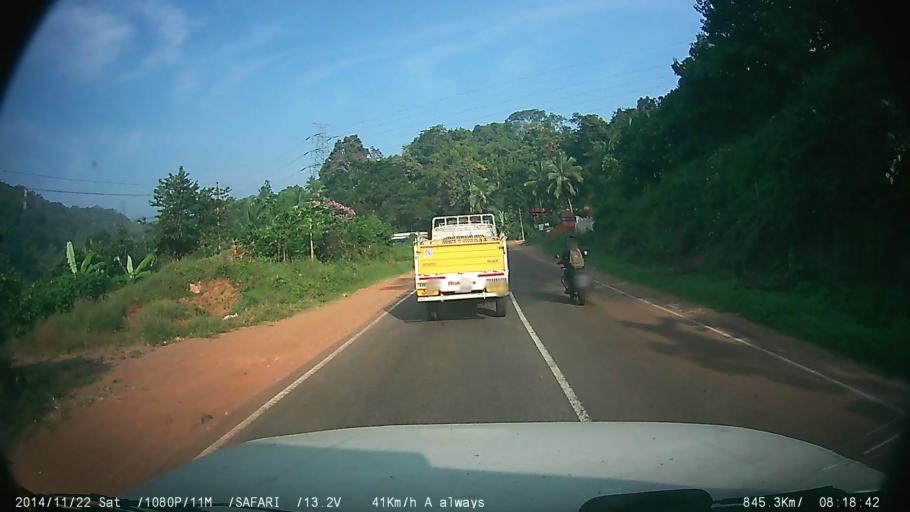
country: IN
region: Kerala
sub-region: Thrissur District
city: Chelakara
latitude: 10.5732
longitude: 76.3895
